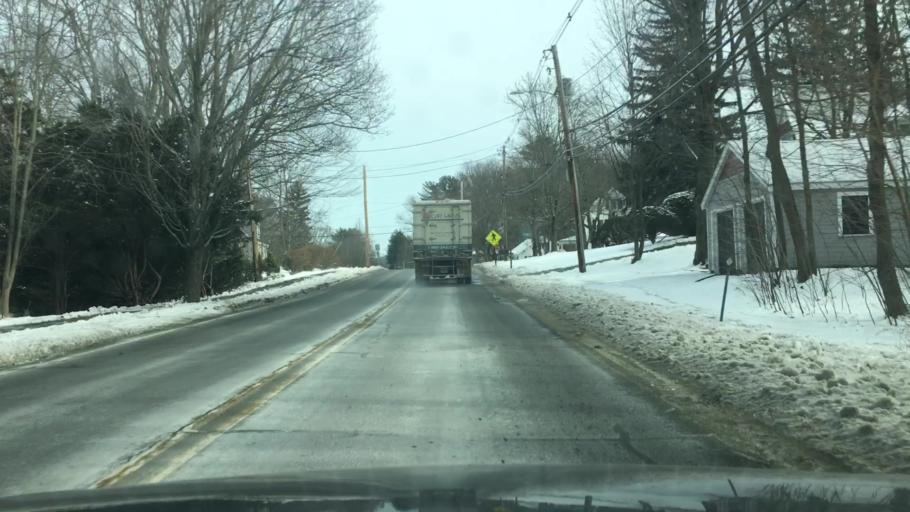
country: US
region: Massachusetts
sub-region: Essex County
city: Middleton
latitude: 42.5952
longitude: -71.0089
